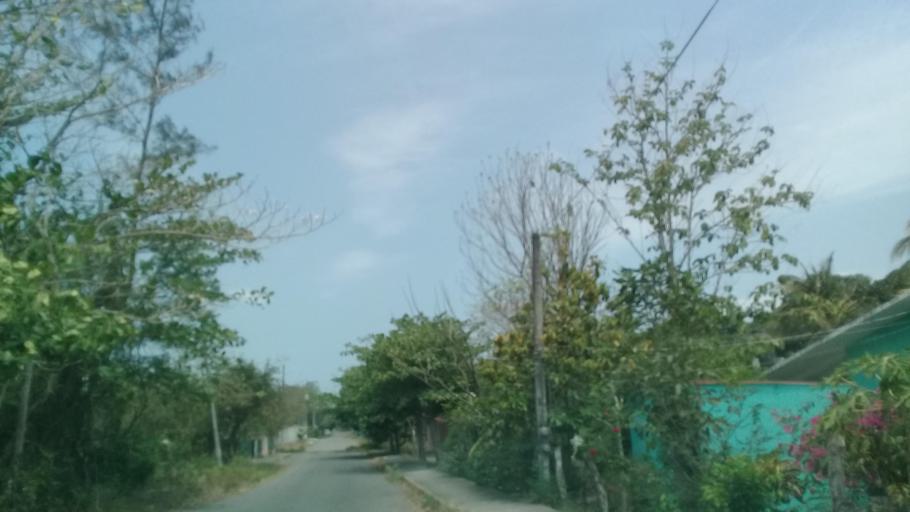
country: MX
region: Veracruz
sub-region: Veracruz
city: Delfino Victoria (Santa Fe)
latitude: 19.1720
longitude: -96.2987
